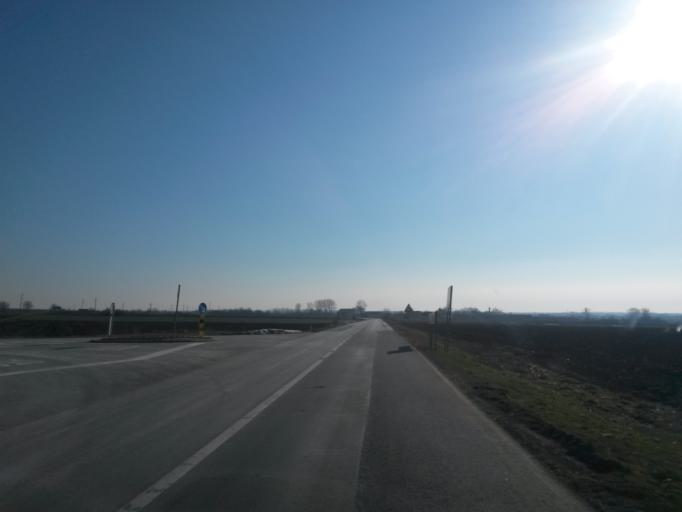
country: HR
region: Osjecko-Baranjska
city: Dalj
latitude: 45.5029
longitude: 18.9557
